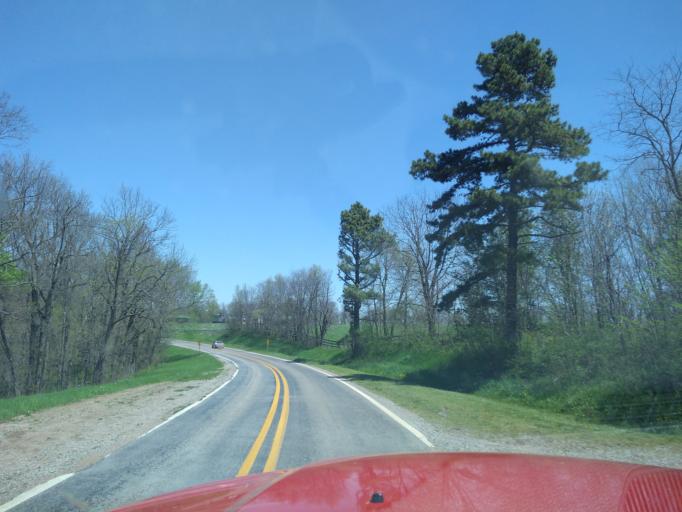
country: US
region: Arkansas
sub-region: Washington County
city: West Fork
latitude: 35.8851
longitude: -94.2406
